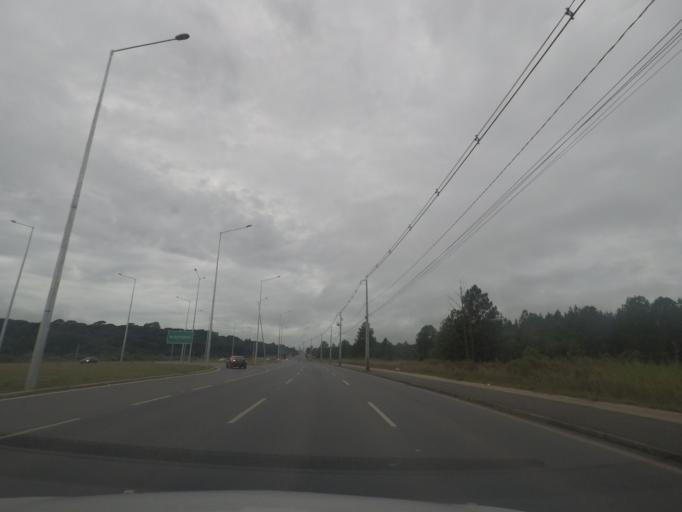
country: BR
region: Parana
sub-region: Piraquara
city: Piraquara
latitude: -25.4521
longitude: -49.1198
